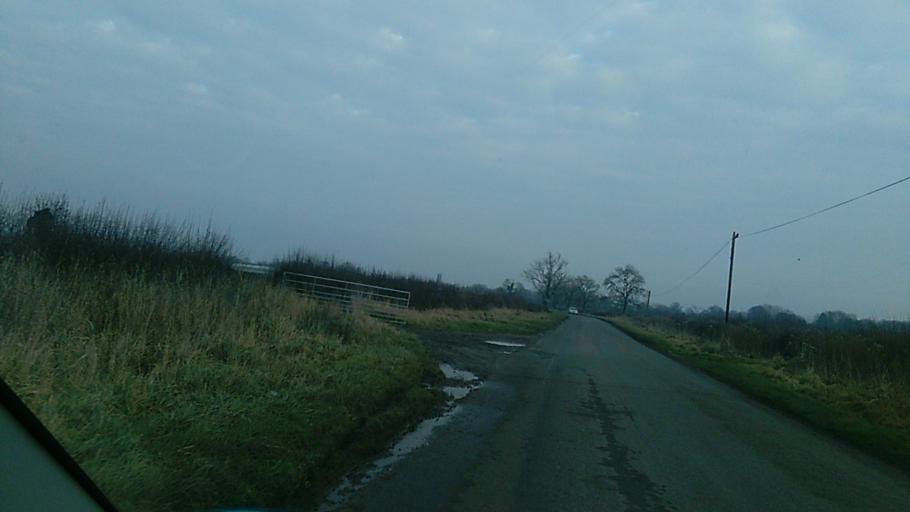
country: GB
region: England
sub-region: Leicestershire
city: Grimston
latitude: 52.8523
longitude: -0.9854
